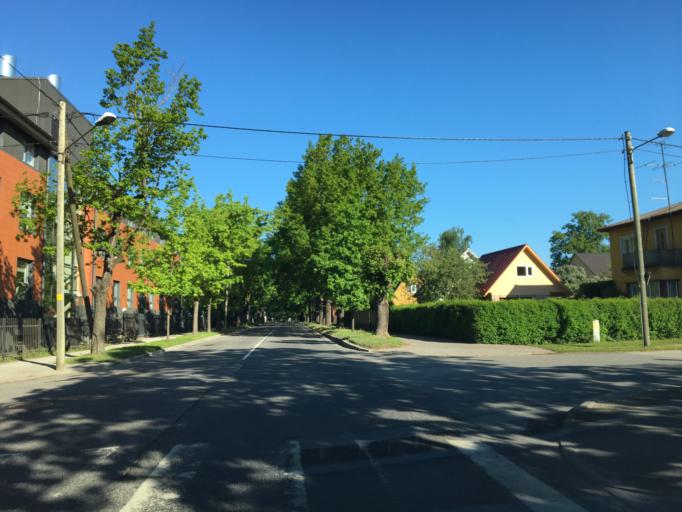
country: EE
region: Tartu
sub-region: Tartu linn
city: Tartu
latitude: 58.3912
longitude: 26.7244
